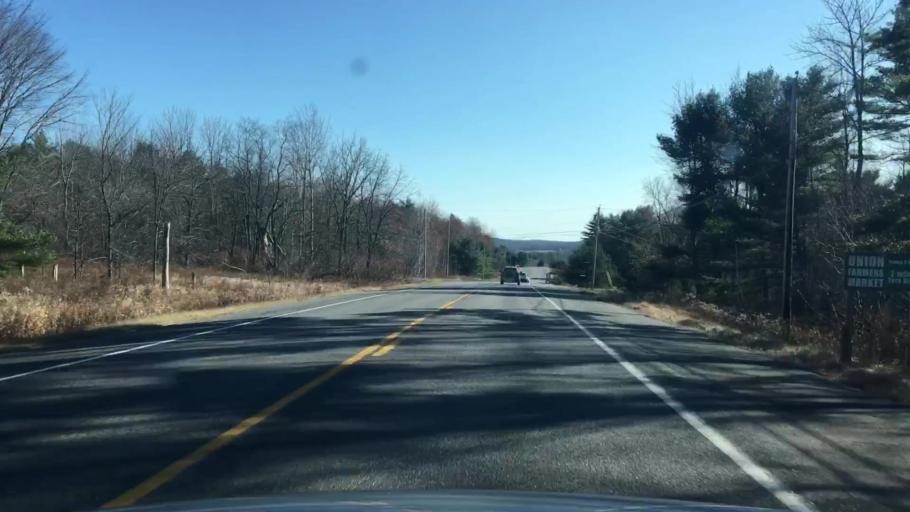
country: US
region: Maine
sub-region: Knox County
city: Union
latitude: 44.2205
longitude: -69.3189
